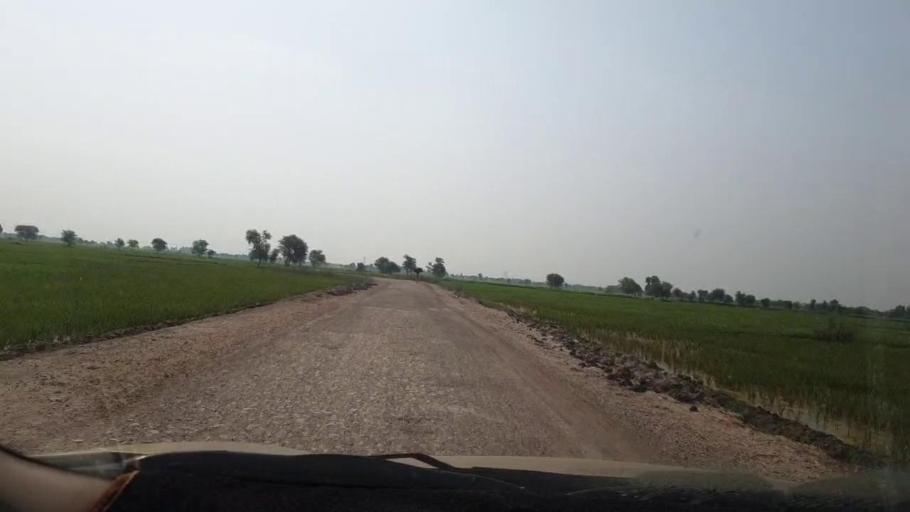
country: PK
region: Sindh
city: Goth Garelo
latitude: 27.4457
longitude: 68.0361
